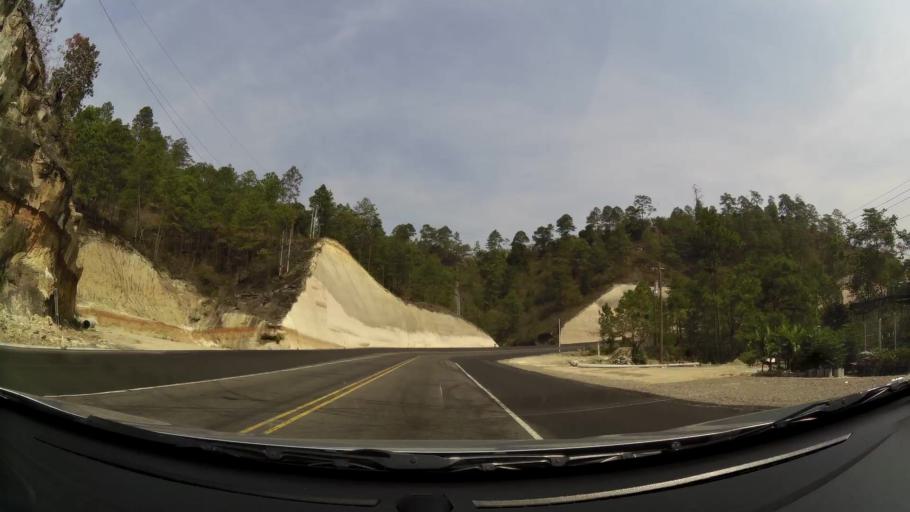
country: HN
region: Comayagua
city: Potrerillos
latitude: 14.5520
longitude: -87.8207
